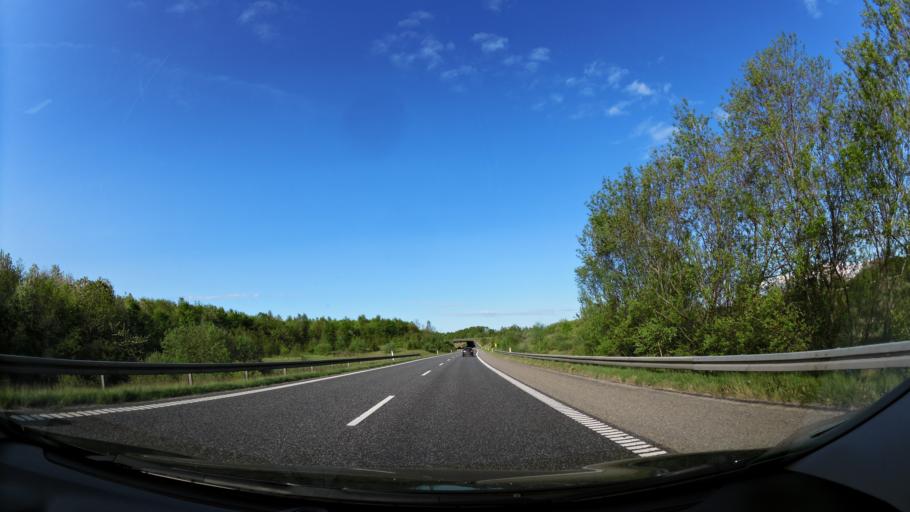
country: DK
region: Central Jutland
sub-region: Skanderborg Kommune
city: Horning
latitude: 56.1041
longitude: 10.0424
